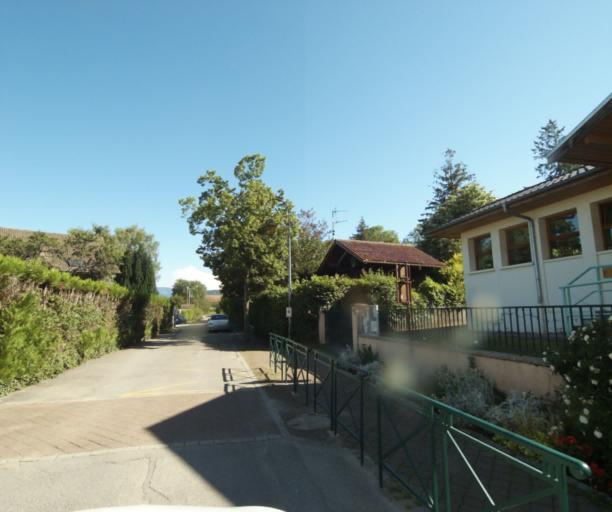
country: FR
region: Rhone-Alpes
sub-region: Departement de la Haute-Savoie
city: Sciez
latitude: 46.3545
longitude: 6.3527
